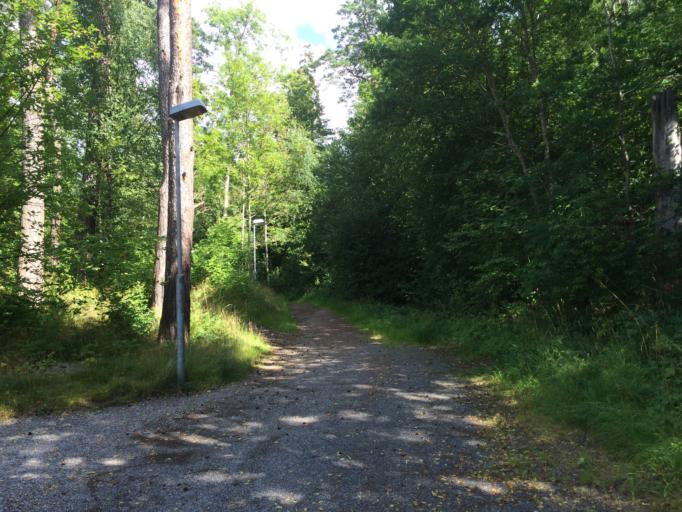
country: SE
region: Stockholm
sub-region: Nacka Kommun
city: Nacka
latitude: 59.3304
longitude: 18.1358
